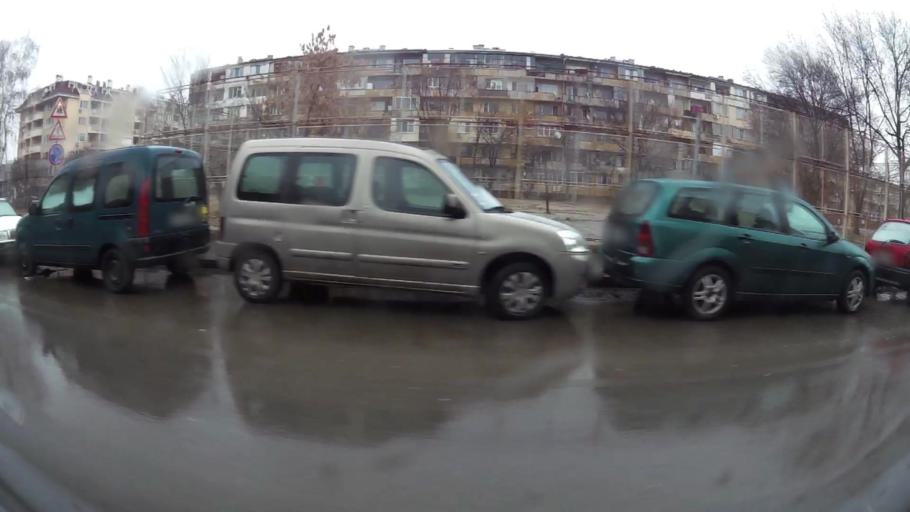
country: BG
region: Sofia-Capital
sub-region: Stolichna Obshtina
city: Sofia
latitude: 42.6632
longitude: 23.3953
